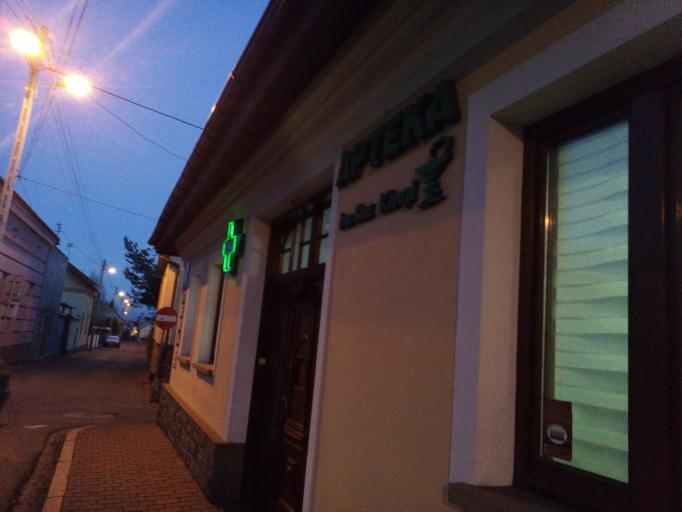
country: PL
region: Lesser Poland Voivodeship
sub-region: Powiat nowosadecki
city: Stary Sacz
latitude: 49.5645
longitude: 20.6340
